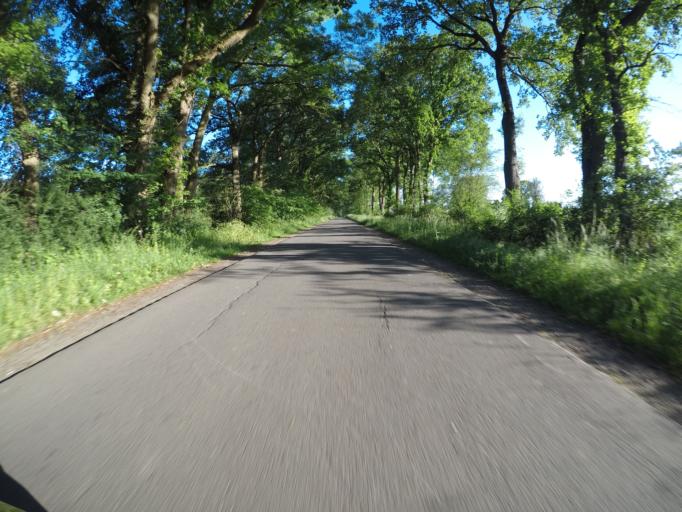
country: DE
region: North Rhine-Westphalia
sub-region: Regierungsbezirk Dusseldorf
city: Schermbeck
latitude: 51.7139
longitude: 6.8553
